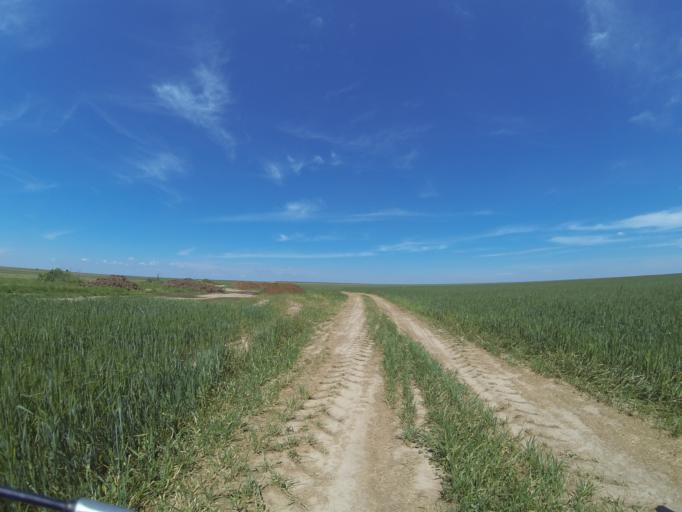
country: RO
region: Dolj
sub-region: Comuna Teslui
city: Teslui
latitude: 44.1835
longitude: 24.1720
